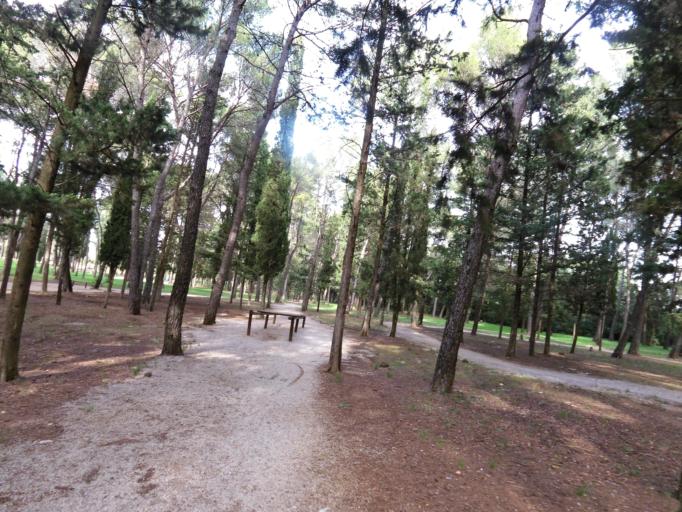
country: FR
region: Languedoc-Roussillon
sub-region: Departement de l'Herault
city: Lunel
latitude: 43.6914
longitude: 4.1283
